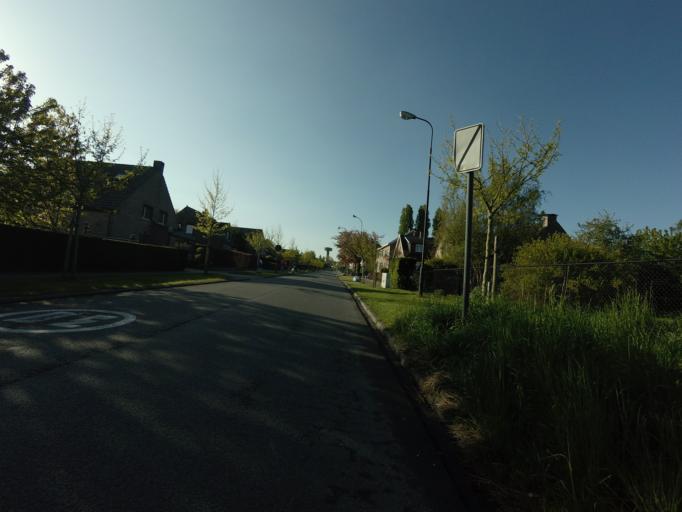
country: BE
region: Flanders
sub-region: Provincie Vlaams-Brabant
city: Grimbergen
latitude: 50.9103
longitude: 4.3736
